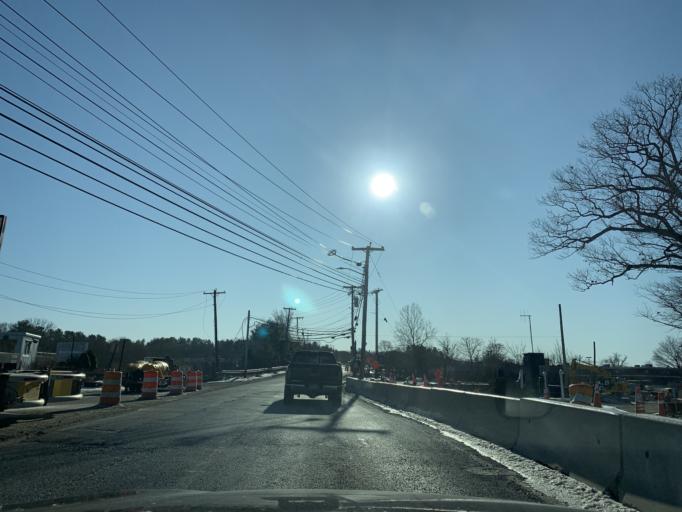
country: US
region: Massachusetts
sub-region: Norfolk County
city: Canton
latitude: 42.1948
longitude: -71.1528
